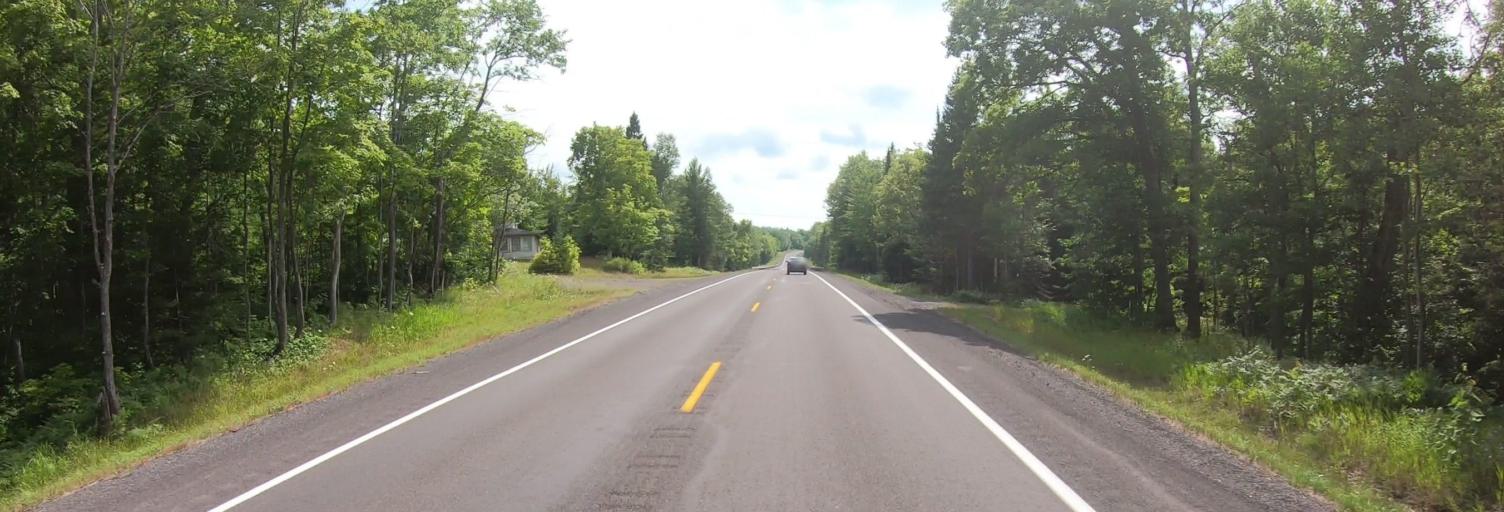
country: US
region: Michigan
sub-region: Houghton County
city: Hancock
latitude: 46.9576
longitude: -88.7788
